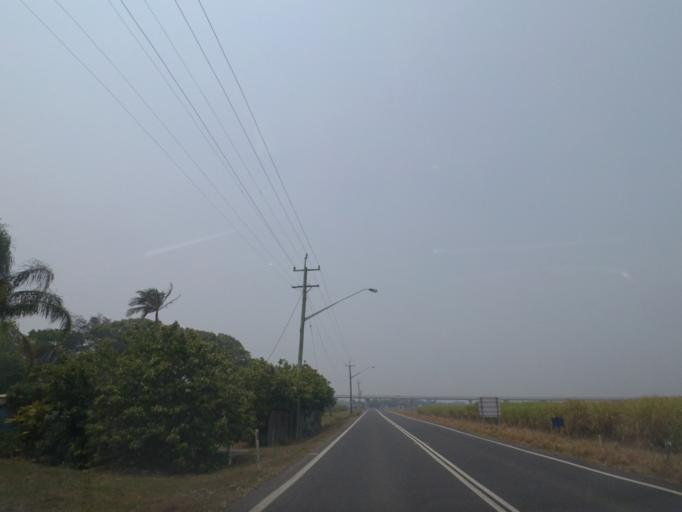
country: AU
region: New South Wales
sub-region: Richmond Valley
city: Evans Head
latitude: -29.0017
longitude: 153.4374
